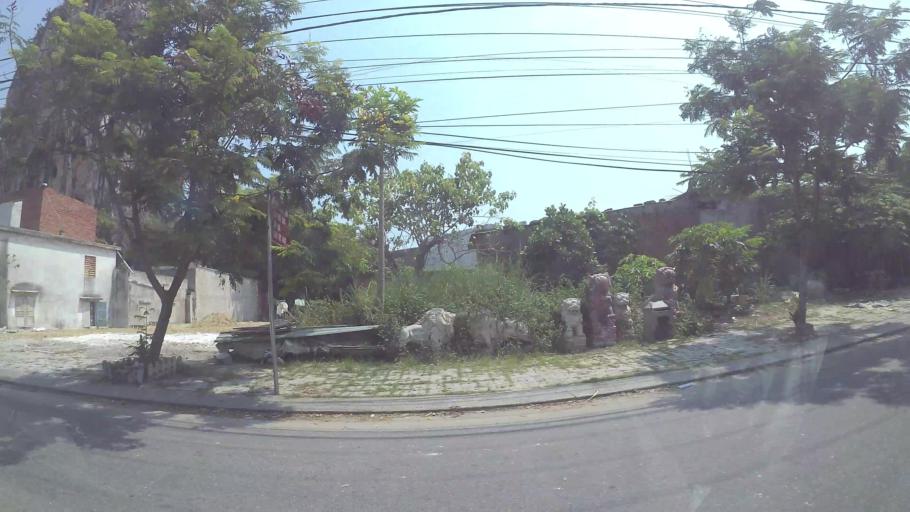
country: VN
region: Da Nang
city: Ngu Hanh Son
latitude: 16.0007
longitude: 108.2600
